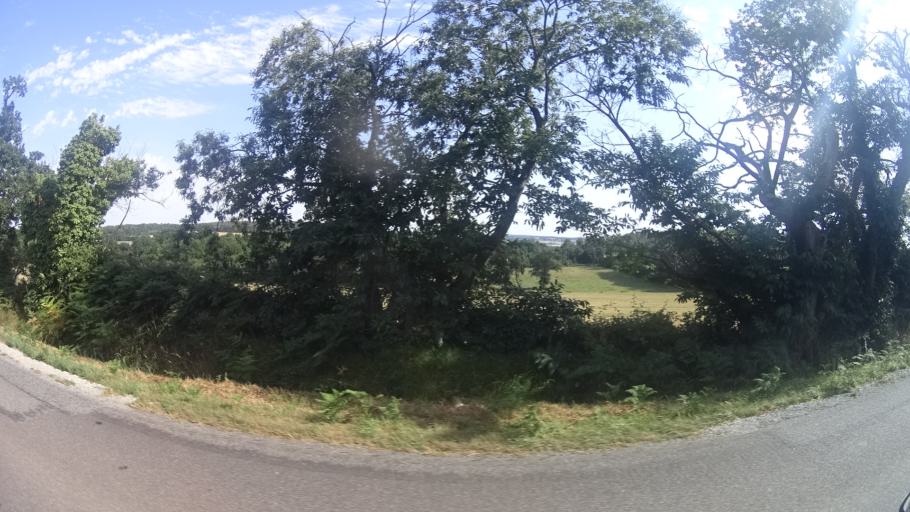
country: FR
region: Brittany
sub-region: Departement du Morbihan
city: Allaire
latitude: 47.6123
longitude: -2.1586
